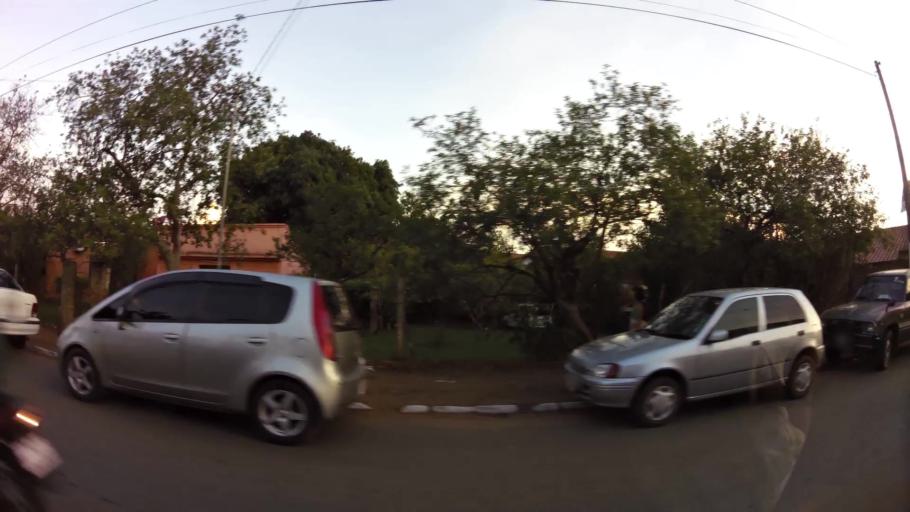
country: PY
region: Central
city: Nemby
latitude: -25.3908
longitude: -57.5030
